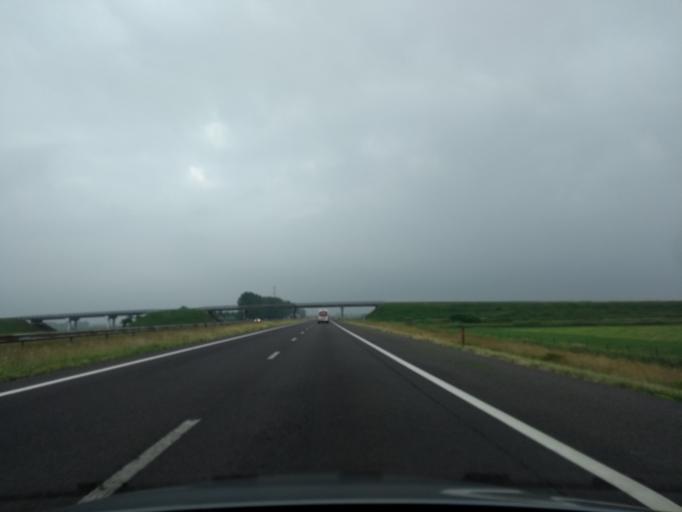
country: NL
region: Friesland
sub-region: Sudwest Fryslan
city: Oppenhuizen
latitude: 52.9875
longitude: 5.7251
